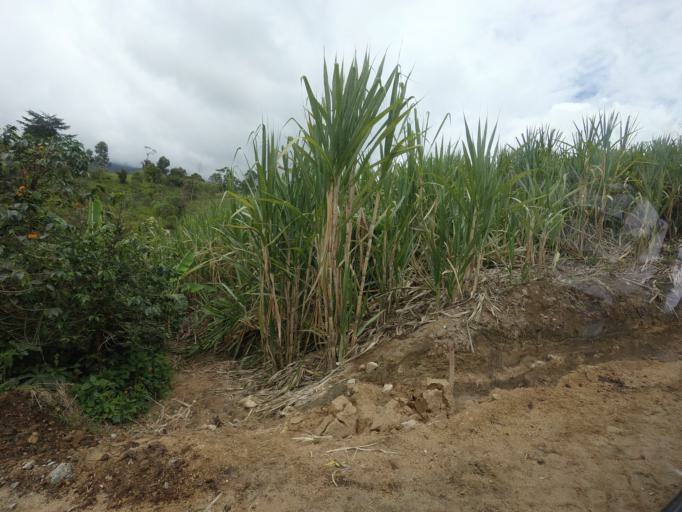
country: CO
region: Huila
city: San Agustin
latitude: 1.9580
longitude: -76.2949
